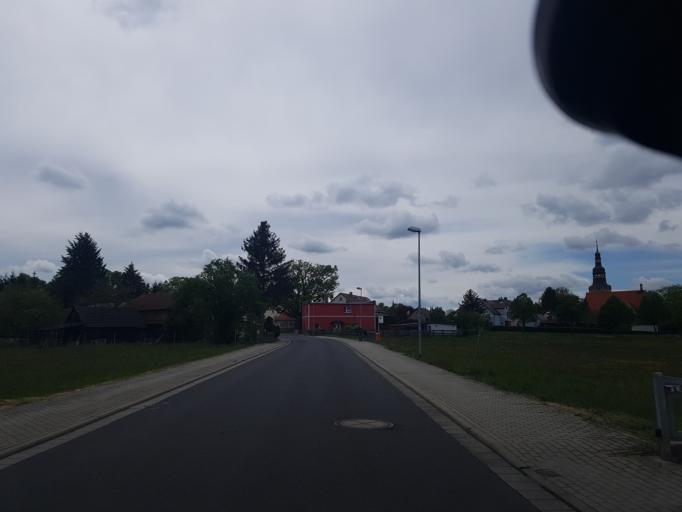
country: DE
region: Brandenburg
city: Tschernitz
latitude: 51.6188
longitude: 14.6023
